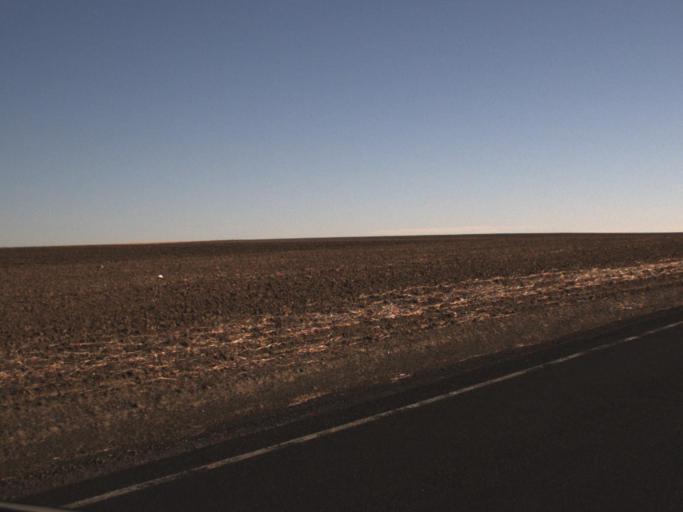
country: US
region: Washington
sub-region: Adams County
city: Ritzville
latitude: 47.0996
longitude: -118.3655
